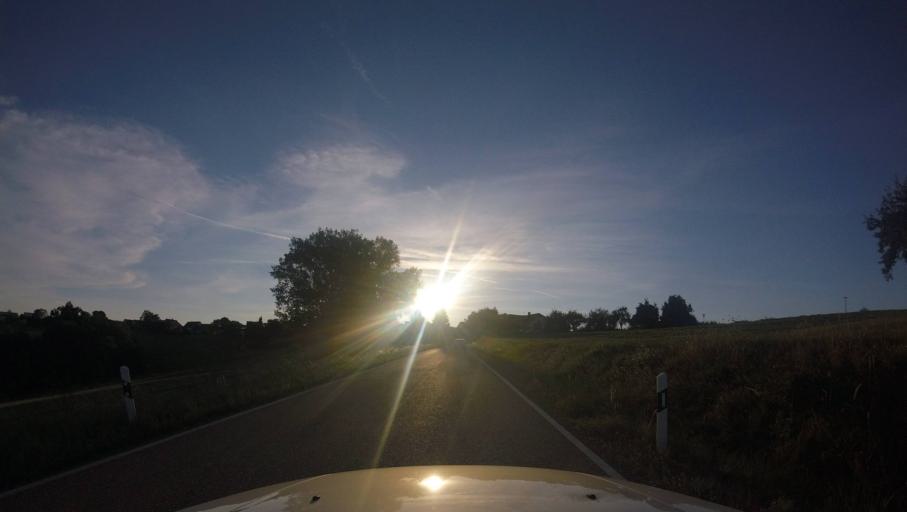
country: DE
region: Baden-Wuerttemberg
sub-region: Regierungsbezirk Stuttgart
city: Kaisersbach
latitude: 48.9284
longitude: 9.6449
